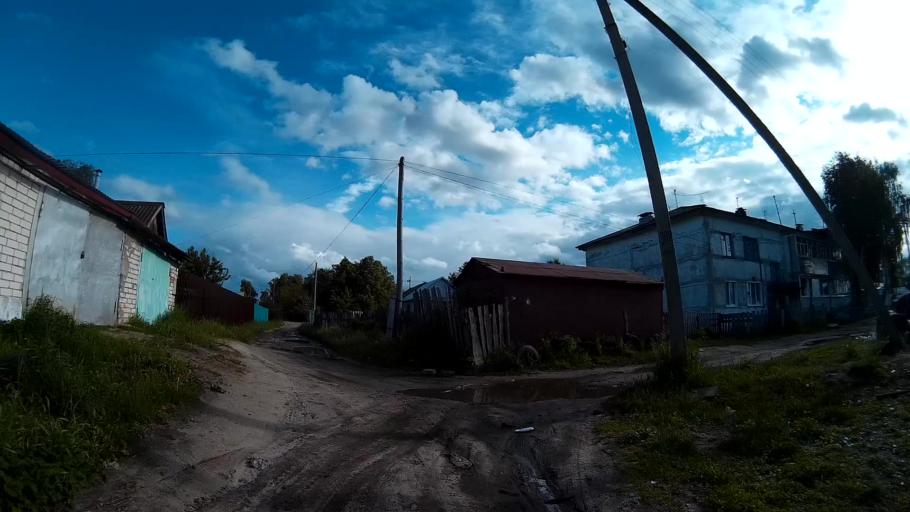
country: RU
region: Ulyanovsk
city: Novoul'yanovsk
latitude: 54.2072
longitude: 48.2662
